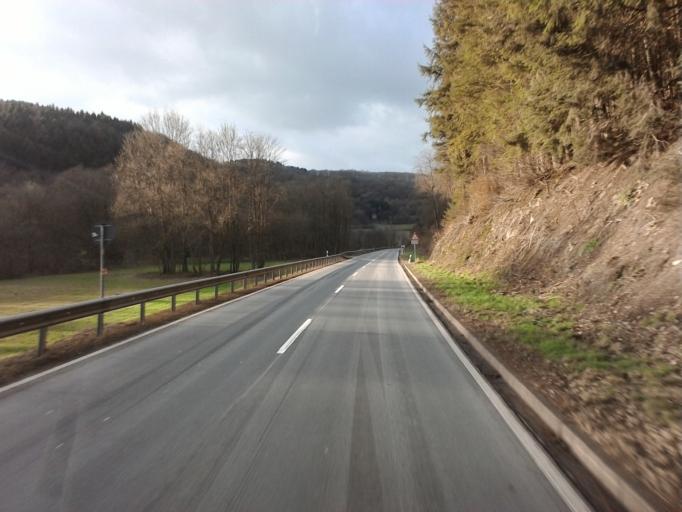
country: DE
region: Rheinland-Pfalz
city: Niederraden
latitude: 49.9892
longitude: 6.3108
